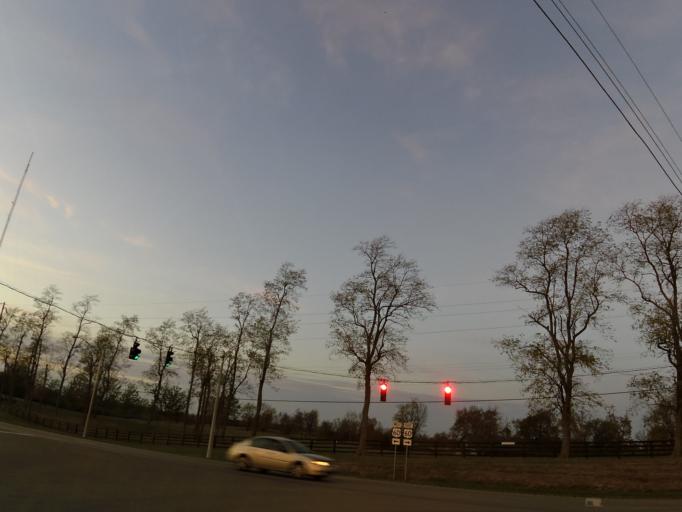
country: US
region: Kentucky
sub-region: Fayette County
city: Lexington-Fayette
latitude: 38.0358
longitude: -84.3969
